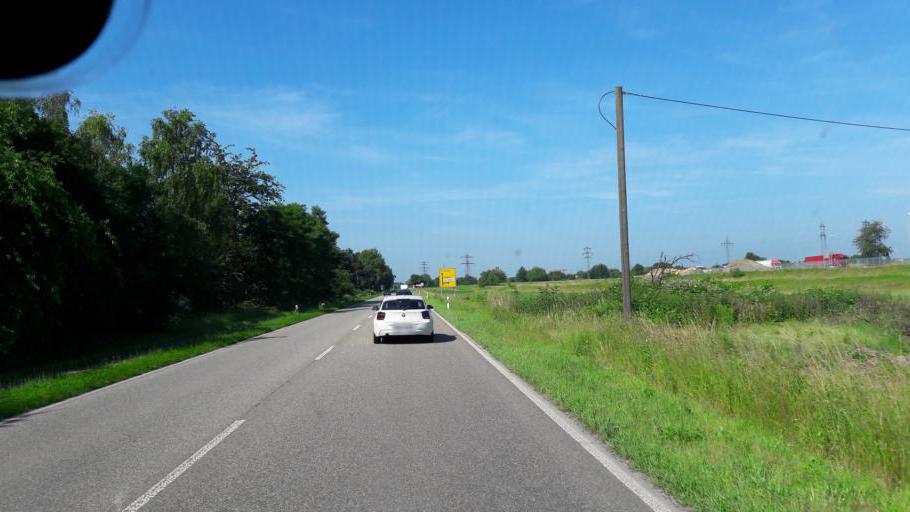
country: DE
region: Baden-Wuerttemberg
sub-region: Karlsruhe Region
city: Muggensturm
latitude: 48.8833
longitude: 8.2648
